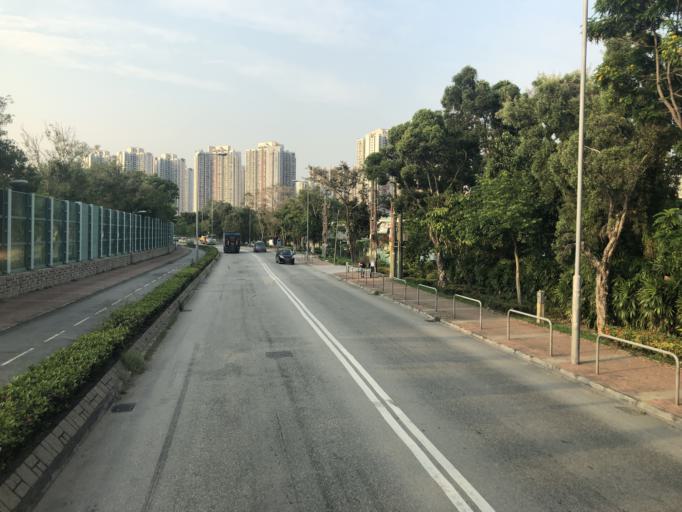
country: HK
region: Yuen Long
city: Yuen Long Kau Hui
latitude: 22.4496
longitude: 113.9944
